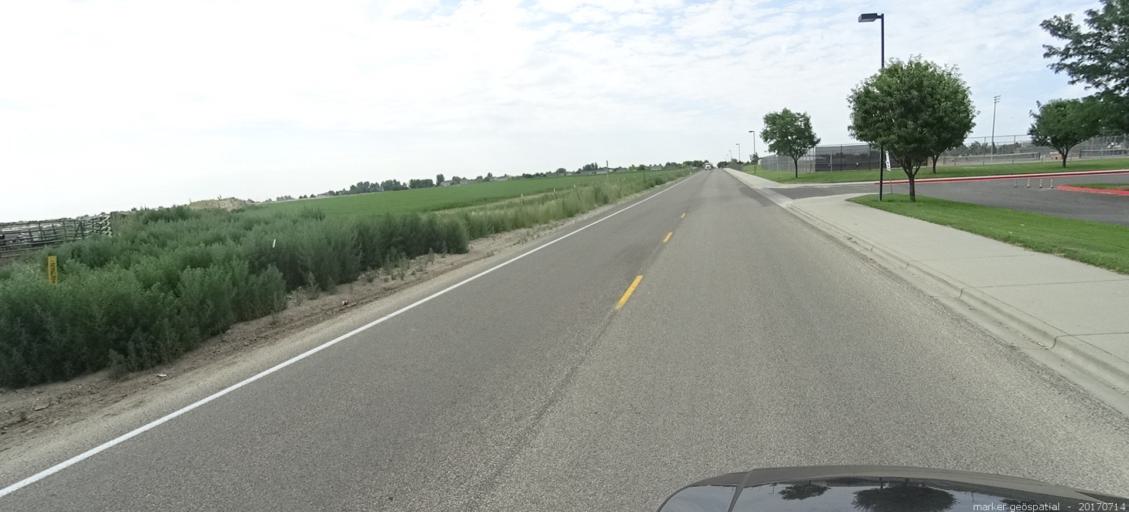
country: US
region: Idaho
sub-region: Ada County
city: Kuna
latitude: 43.5017
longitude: -116.4039
